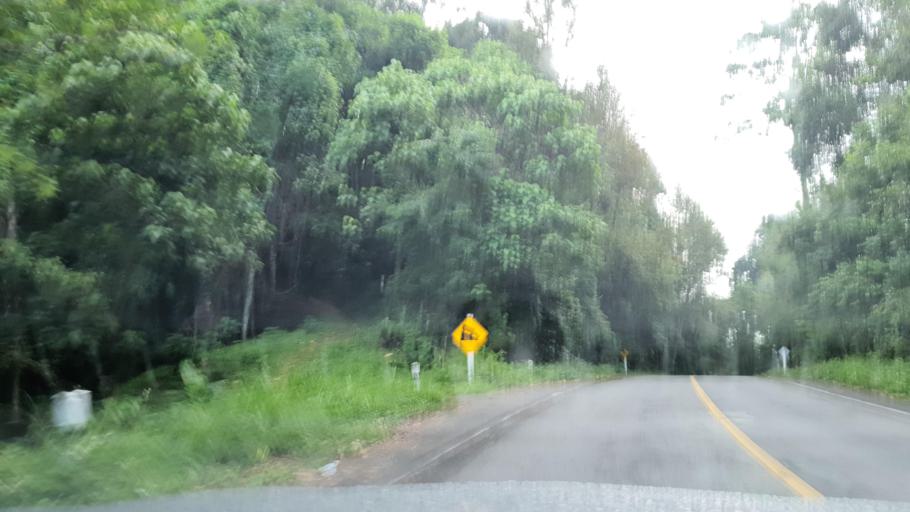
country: TH
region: Chiang Mai
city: Mae On
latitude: 18.9935
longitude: 99.3399
